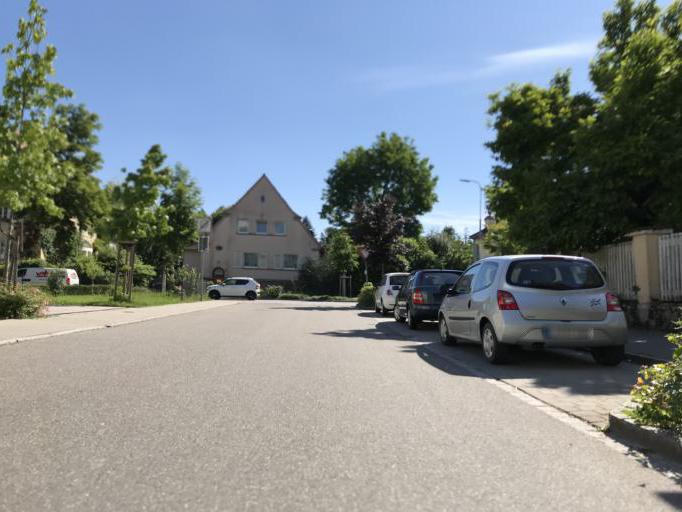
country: DE
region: Baden-Wuerttemberg
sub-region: Freiburg Region
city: Schopfheim
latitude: 47.6465
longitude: 7.8255
